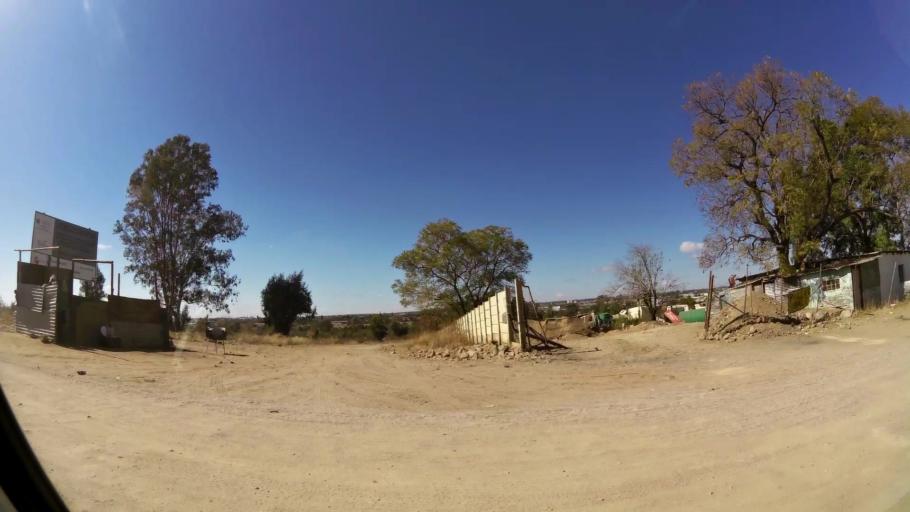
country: ZA
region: Limpopo
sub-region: Capricorn District Municipality
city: Polokwane
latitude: -23.8833
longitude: 29.4251
